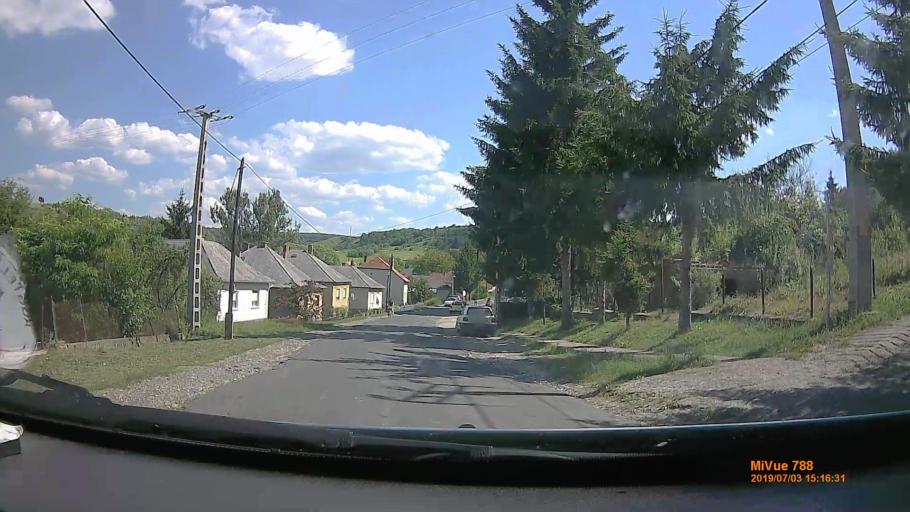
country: HU
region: Borsod-Abauj-Zemplen
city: Farkaslyuk
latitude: 48.2102
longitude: 20.3981
